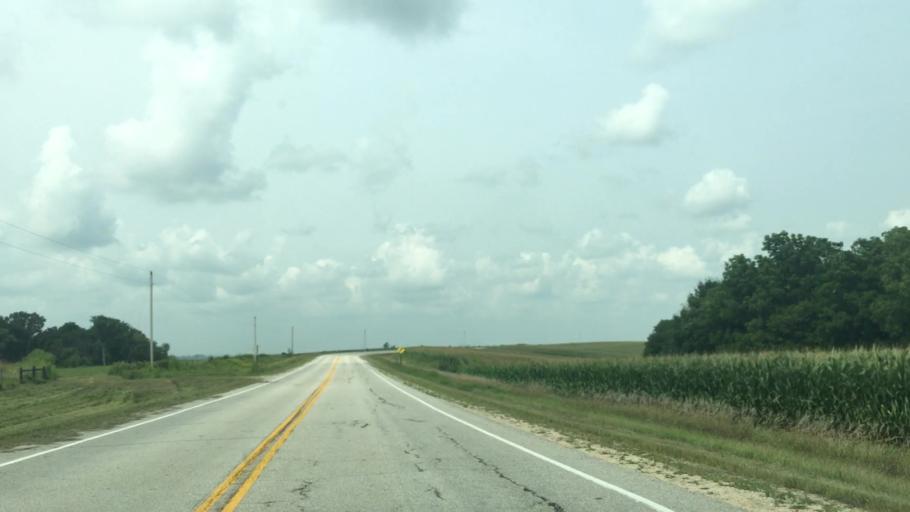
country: US
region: Minnesota
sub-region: Fillmore County
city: Harmony
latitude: 43.6663
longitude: -91.9329
